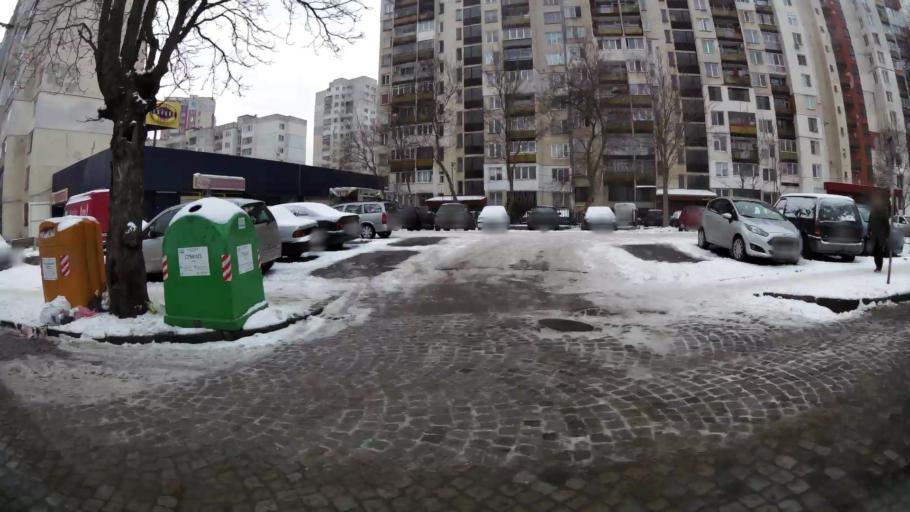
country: BG
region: Sofia-Capital
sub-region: Stolichna Obshtina
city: Sofia
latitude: 42.7103
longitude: 23.3081
